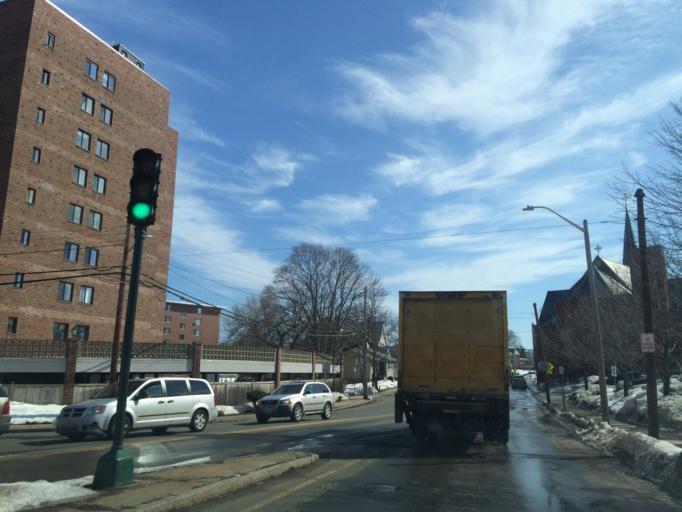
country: US
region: Massachusetts
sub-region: Middlesex County
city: Arlington
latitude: 42.4165
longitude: -71.1513
